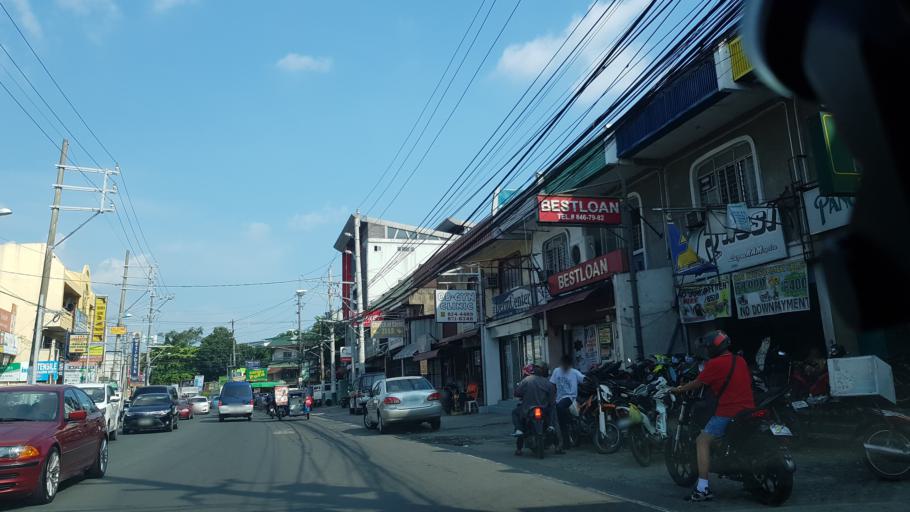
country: PH
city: Sambayanihan People's Village
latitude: 14.4827
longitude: 121.0360
